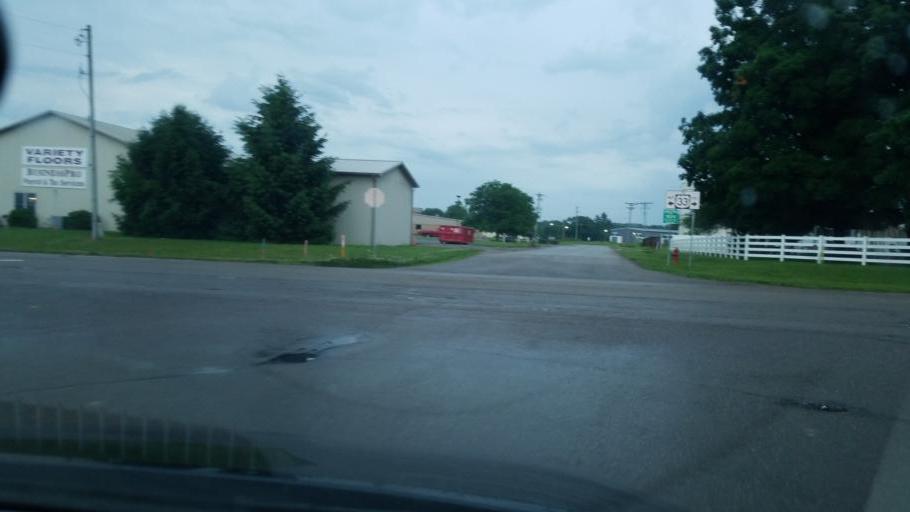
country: US
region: Ohio
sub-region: Fairfield County
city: Lancaster
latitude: 39.7722
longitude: -82.6839
